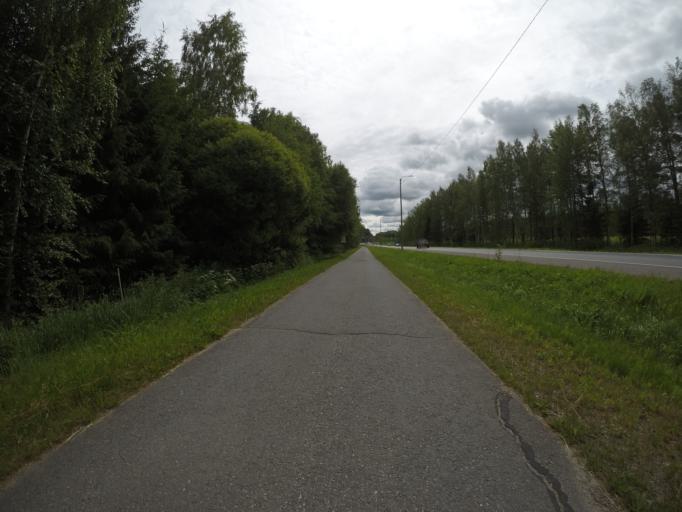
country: FI
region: Haeme
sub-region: Haemeenlinna
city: Haemeenlinna
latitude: 60.9880
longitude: 24.5029
